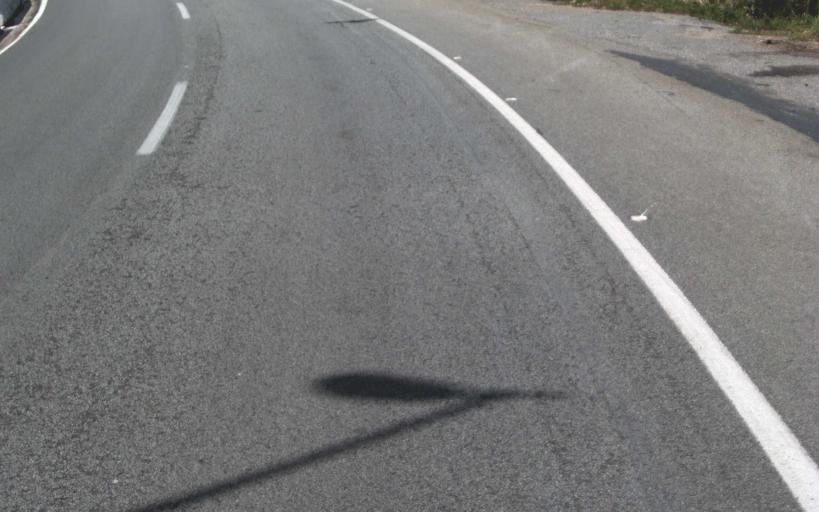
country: BR
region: Minas Gerais
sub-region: Nova Era
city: Nova Era
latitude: -19.7613
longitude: -43.0313
